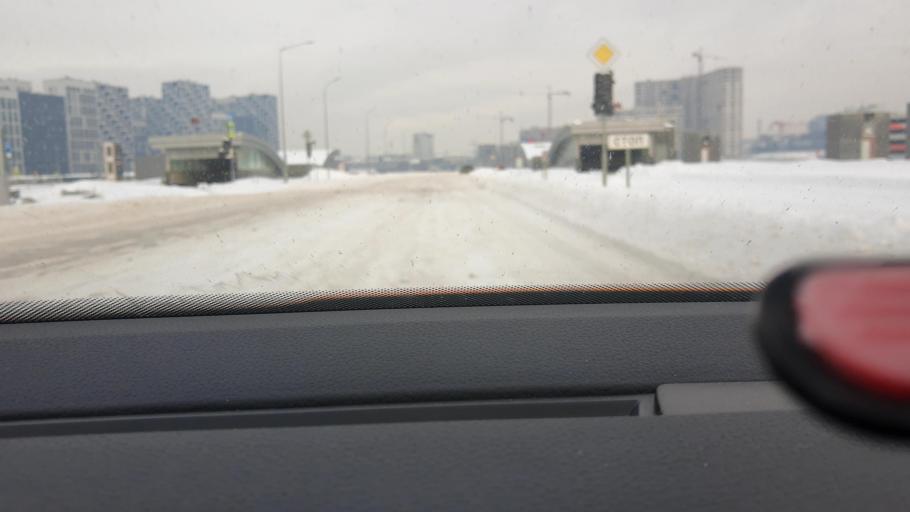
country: RU
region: Moscow
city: Strogino
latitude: 55.8165
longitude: 37.4342
